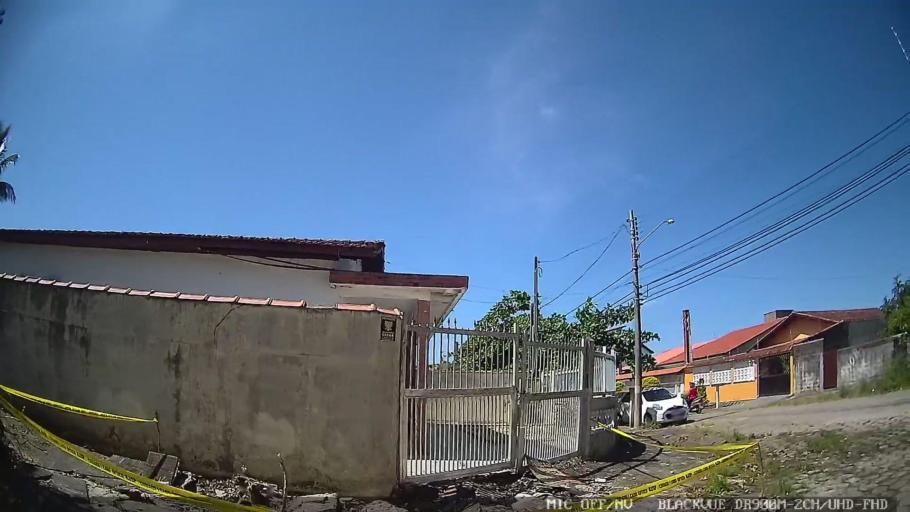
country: BR
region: Sao Paulo
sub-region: Peruibe
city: Peruibe
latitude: -24.3049
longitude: -46.9829
